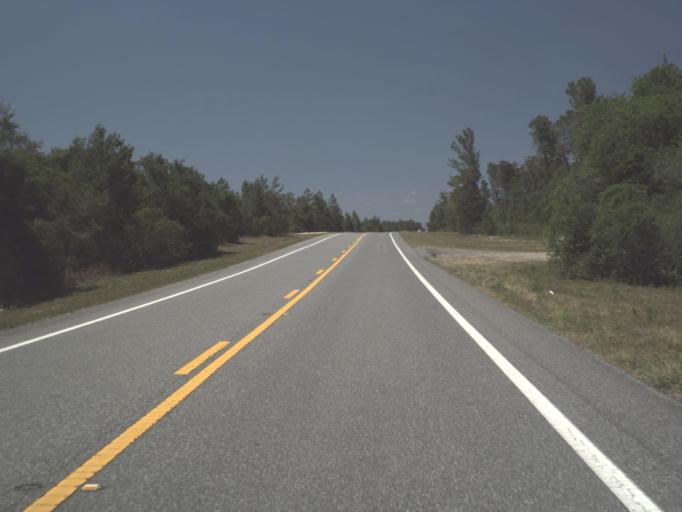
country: US
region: Florida
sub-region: Lake County
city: Astor
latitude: 29.1295
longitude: -81.6224
